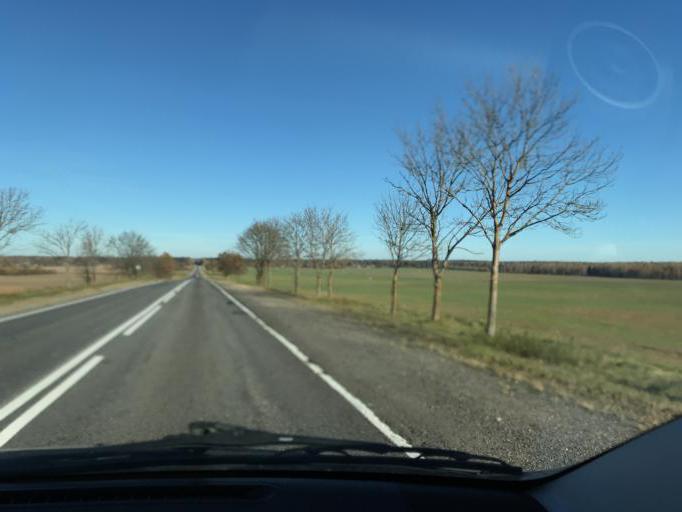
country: BY
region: Vitebsk
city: Lyepyel'
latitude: 55.0426
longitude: 28.7493
